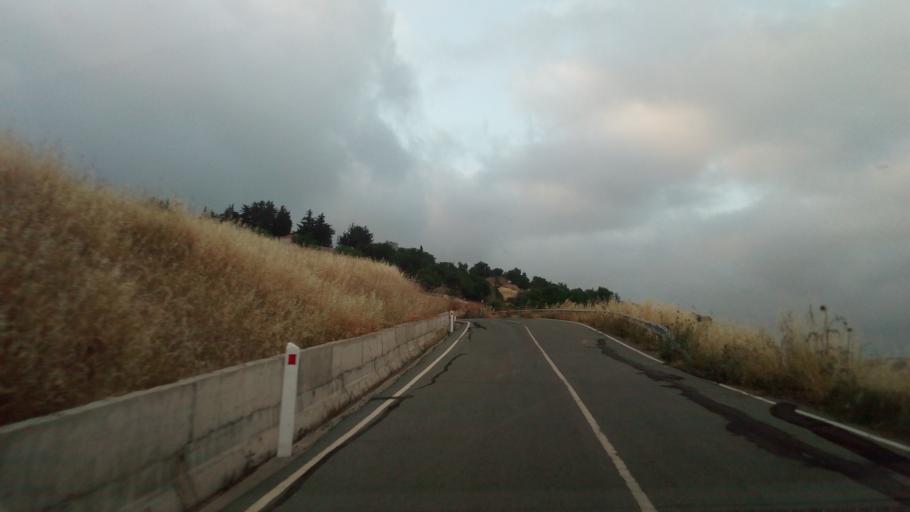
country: CY
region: Pafos
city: Mesogi
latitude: 34.8739
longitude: 32.6315
